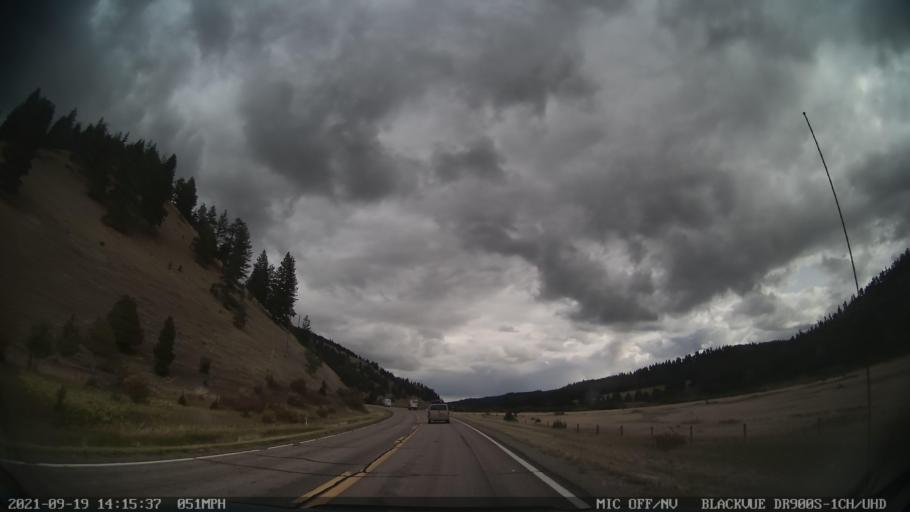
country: US
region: Montana
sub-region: Lewis and Clark County
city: Lincoln
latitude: 46.8194
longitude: -112.8614
